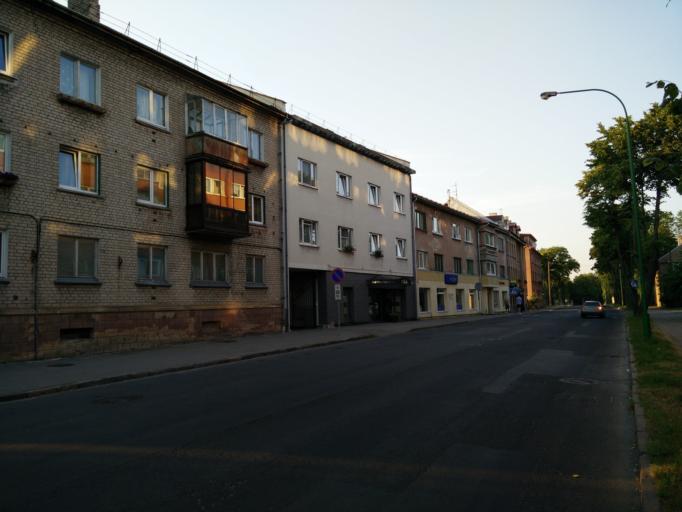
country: LT
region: Klaipedos apskritis
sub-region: Klaipeda
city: Klaipeda
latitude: 55.7089
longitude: 21.1435
